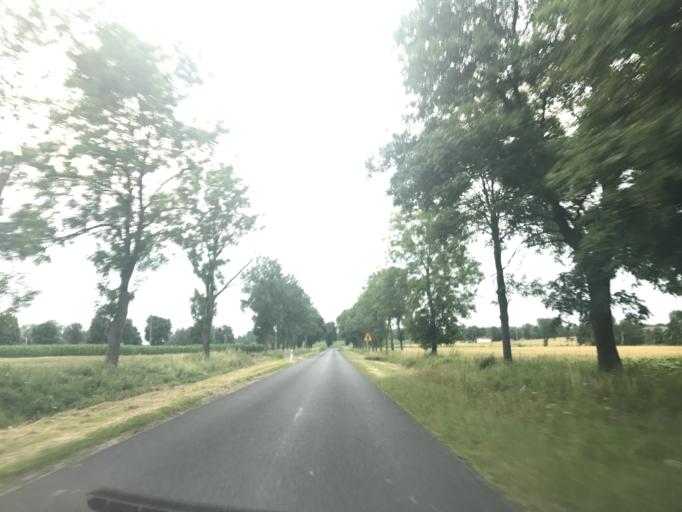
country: PL
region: Kujawsko-Pomorskie
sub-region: Powiat lipnowski
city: Lipno
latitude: 52.8079
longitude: 19.1874
